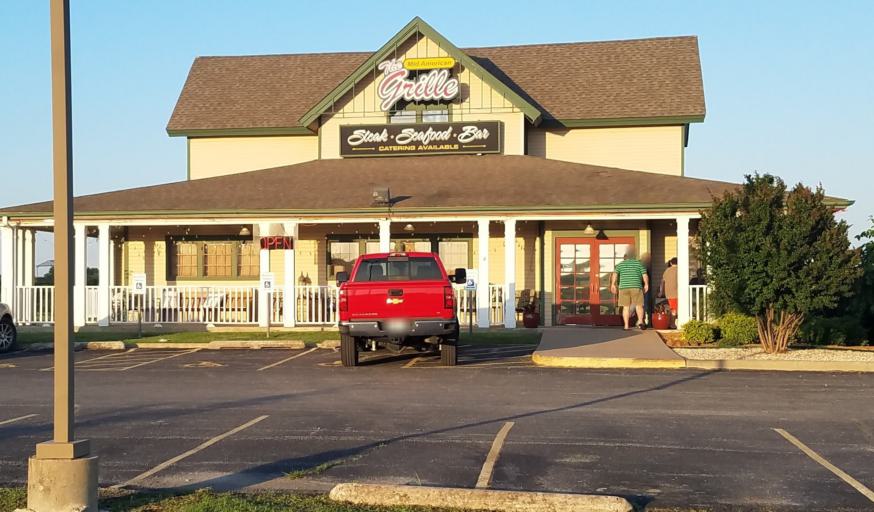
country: US
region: Oklahoma
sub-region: Mayes County
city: Pryor
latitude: 36.2522
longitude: -95.3341
